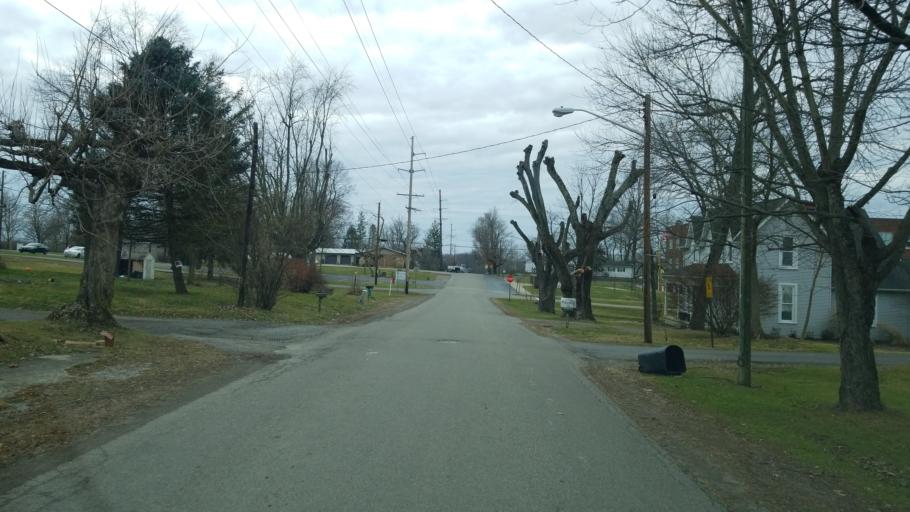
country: US
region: Ohio
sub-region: Highland County
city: Greenfield
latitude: 39.3355
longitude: -83.3085
